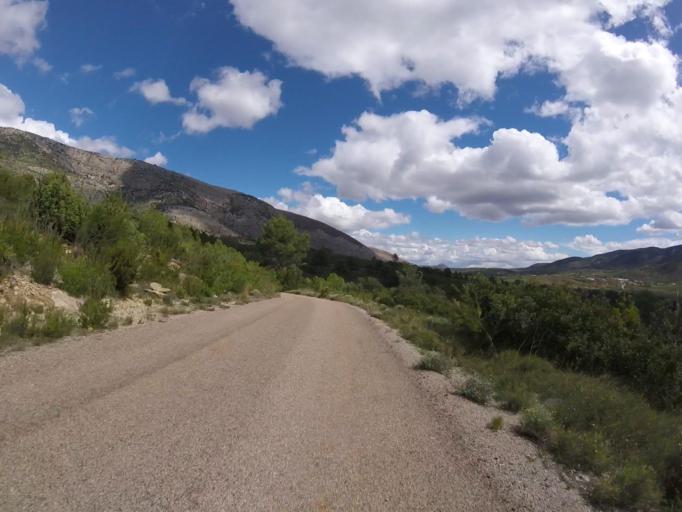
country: ES
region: Valencia
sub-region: Provincia de Castello
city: Sierra-Engarceran
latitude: 40.2847
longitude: -0.0698
